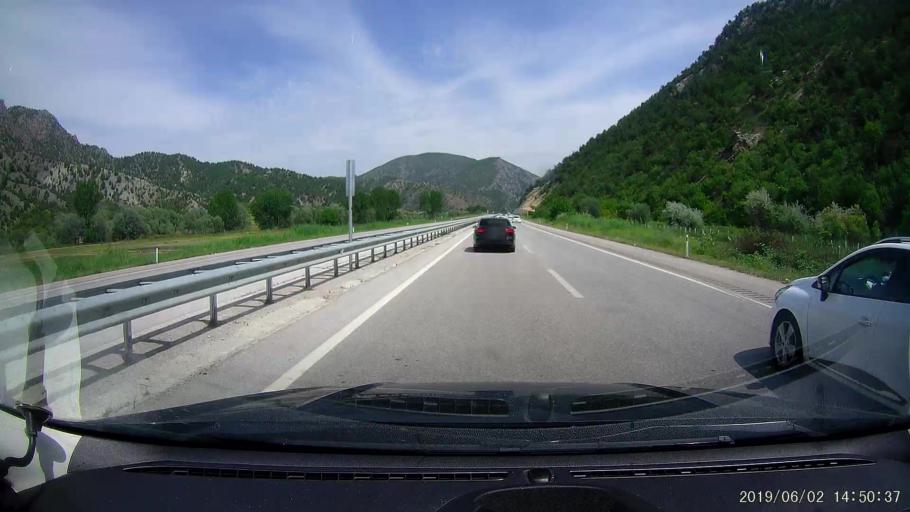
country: TR
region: Corum
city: Kargi
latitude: 41.0704
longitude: 34.5239
